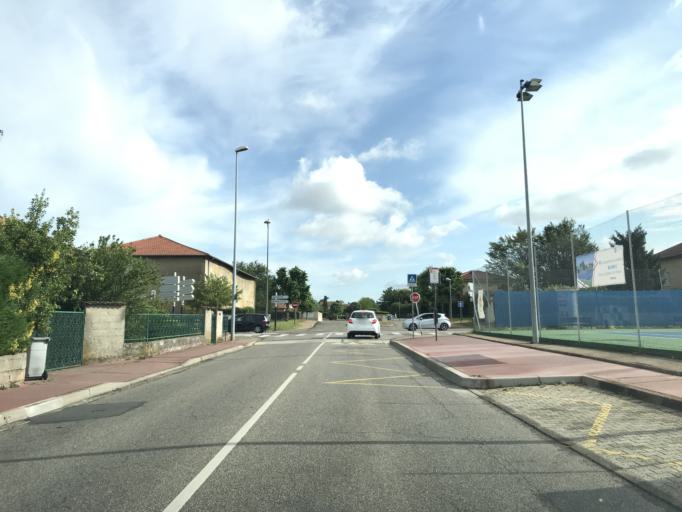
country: FR
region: Rhone-Alpes
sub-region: Departement du Rhone
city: Mions
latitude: 45.6628
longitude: 4.9493
